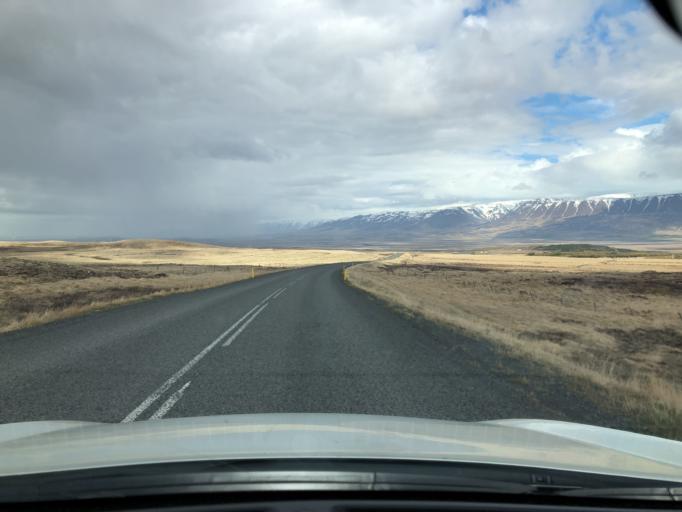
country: IS
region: Northwest
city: Saudarkrokur
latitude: 65.5351
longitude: -19.5109
